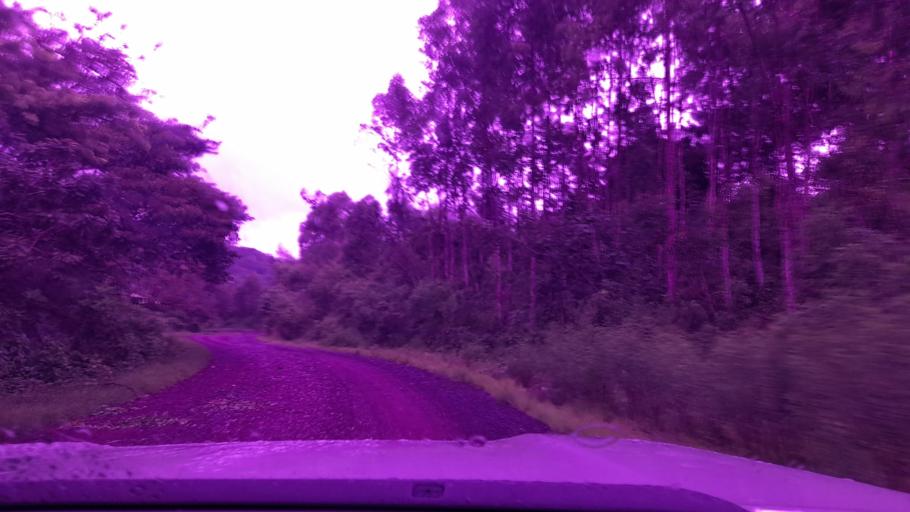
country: ET
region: Oromiya
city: Metu
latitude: 8.4506
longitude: 35.6343
